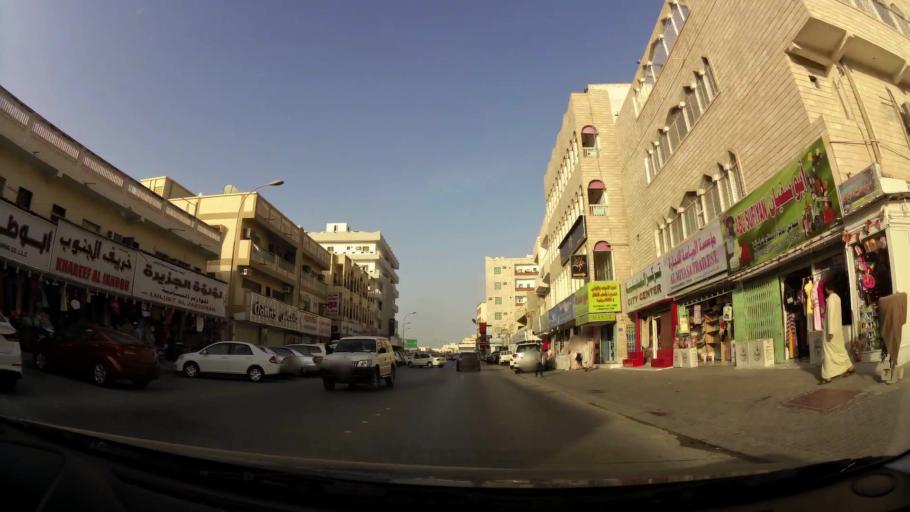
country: OM
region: Zufar
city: Salalah
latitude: 17.0129
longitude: 54.0948
